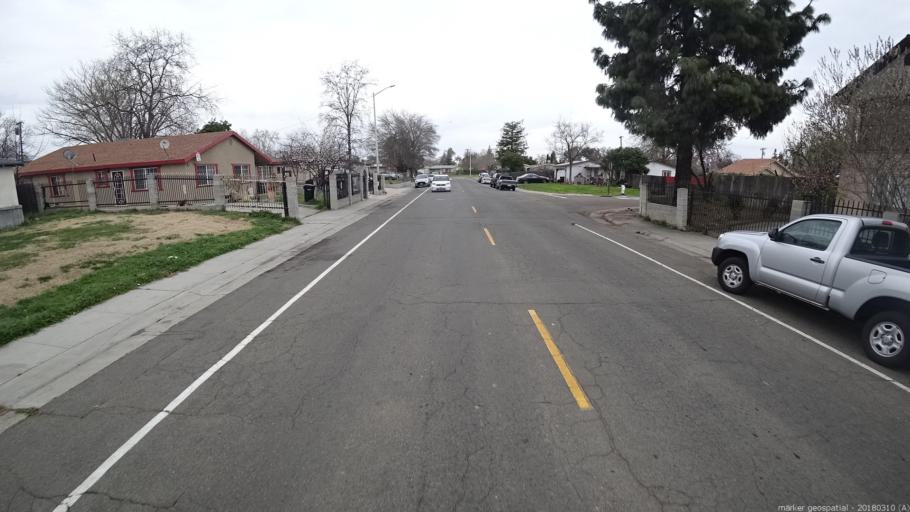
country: US
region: California
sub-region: Sacramento County
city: Florin
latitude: 38.4908
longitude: -121.4035
